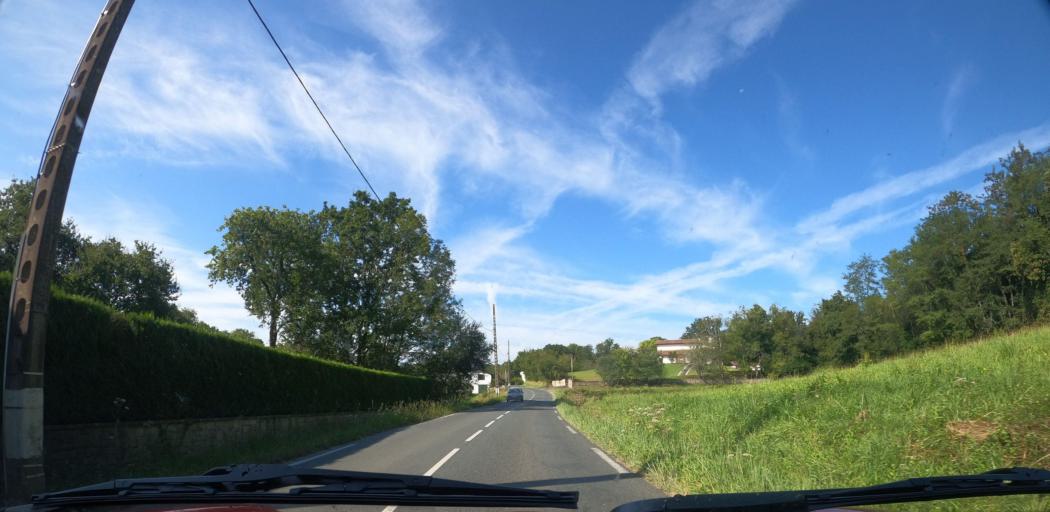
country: FR
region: Aquitaine
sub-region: Departement des Pyrenees-Atlantiques
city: Sare
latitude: 43.3187
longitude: -1.5577
